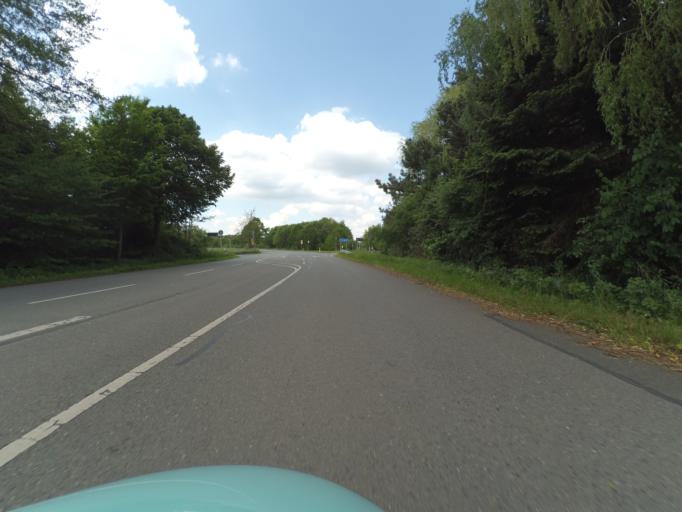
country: DE
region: Lower Saxony
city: Lehrte
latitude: 52.3791
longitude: 10.0200
